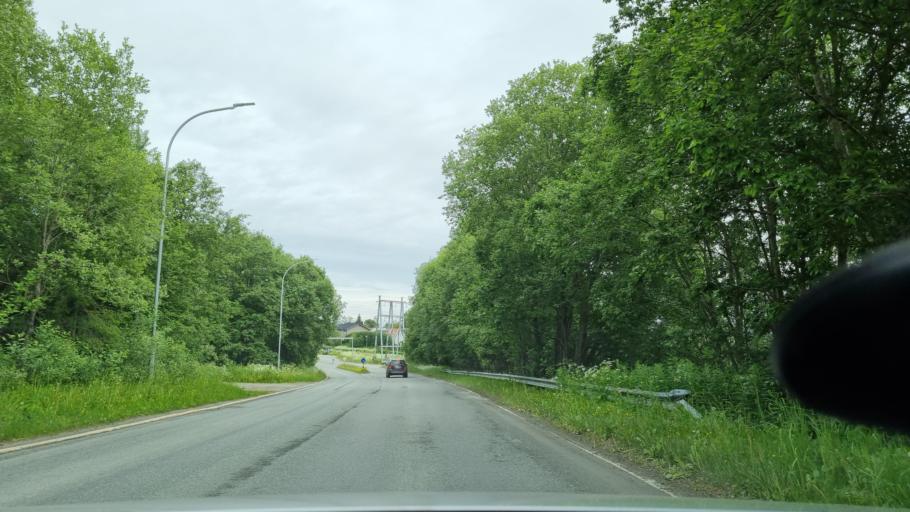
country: NO
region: Sor-Trondelag
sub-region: Trondheim
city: Trondheim
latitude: 63.3577
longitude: 10.3408
